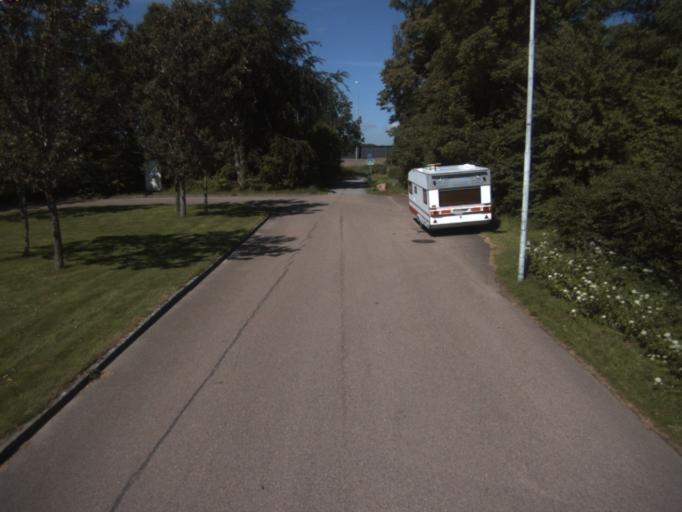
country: SE
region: Skane
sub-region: Helsingborg
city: Odakra
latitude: 56.0757
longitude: 12.7345
